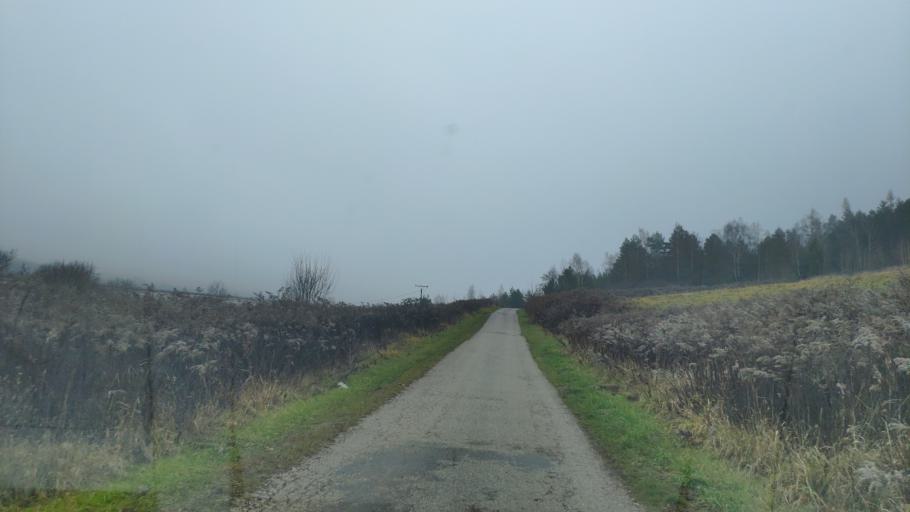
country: SK
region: Banskobystricky
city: Revuca
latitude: 48.6405
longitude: 20.2410
